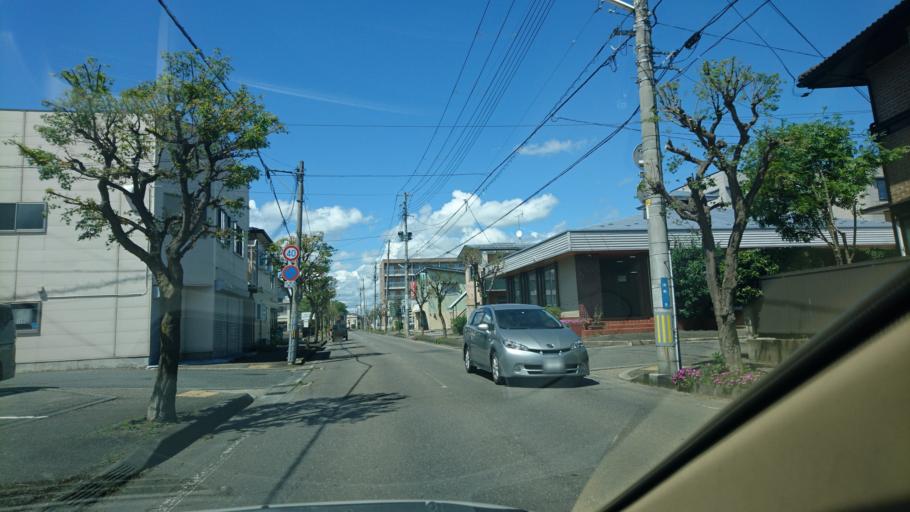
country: JP
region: Iwate
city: Kitakami
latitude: 39.2877
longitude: 141.1092
